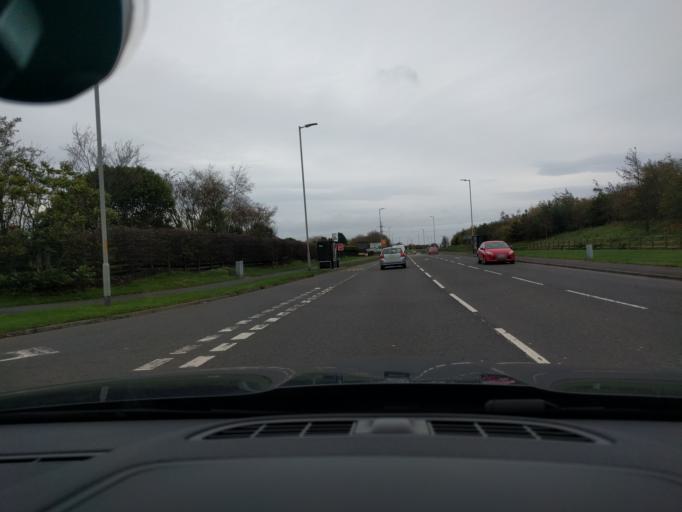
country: GB
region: England
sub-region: Northumberland
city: Newbiggin-by-the-Sea
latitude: 55.1719
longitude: -1.5385
